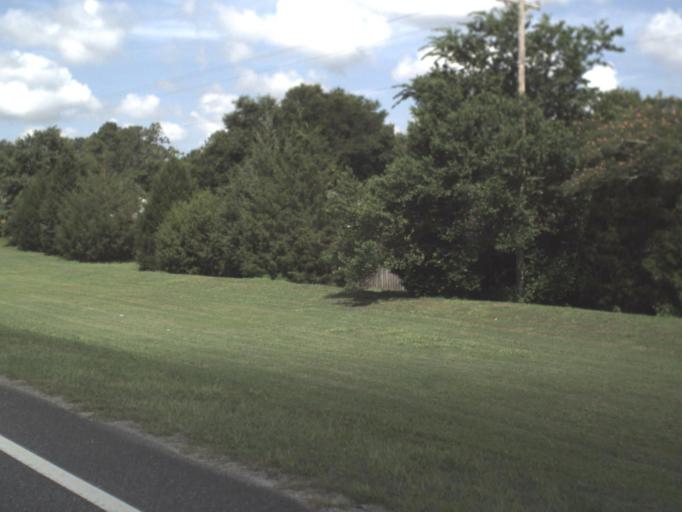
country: US
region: Florida
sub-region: Alachua County
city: Archer
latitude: 29.5941
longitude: -82.4305
